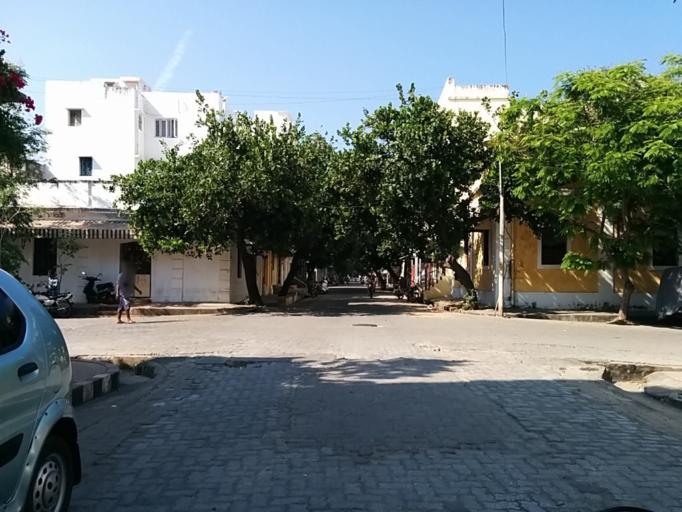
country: IN
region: Pondicherry
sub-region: Puducherry
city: Puducherry
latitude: 11.9375
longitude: 79.8341
